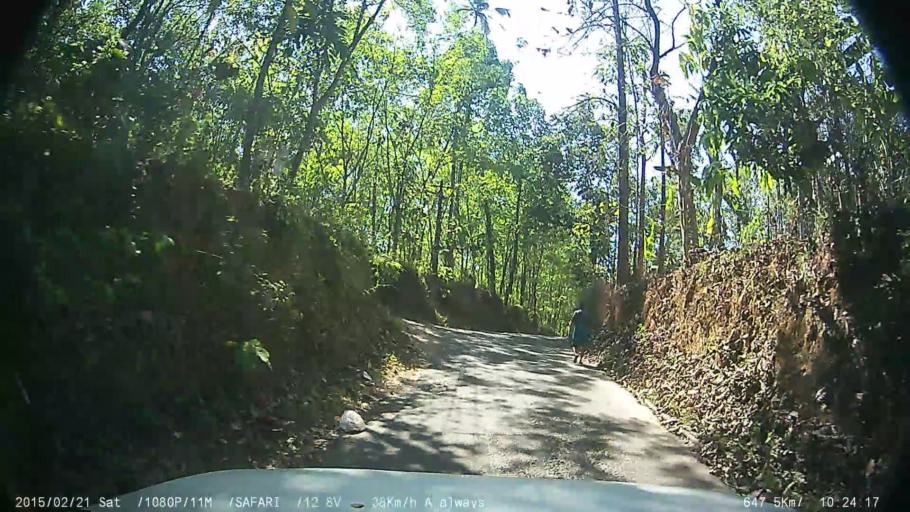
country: IN
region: Kerala
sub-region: Kottayam
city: Palackattumala
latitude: 9.8576
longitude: 76.6792
